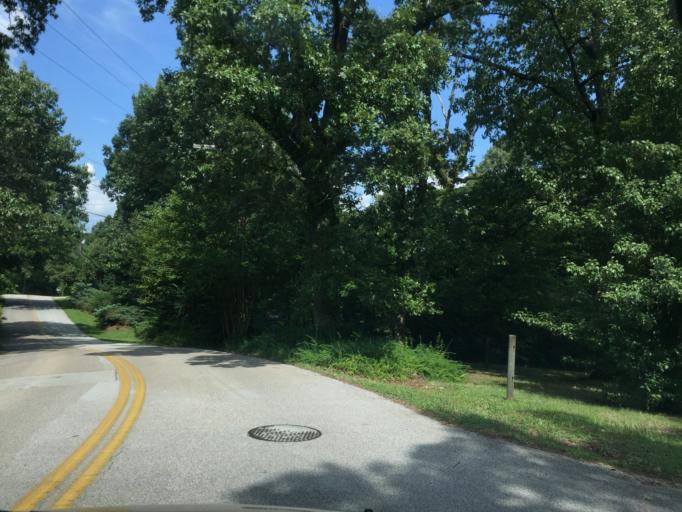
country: US
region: Tennessee
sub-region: Hamilton County
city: East Chattanooga
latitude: 35.0960
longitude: -85.2053
